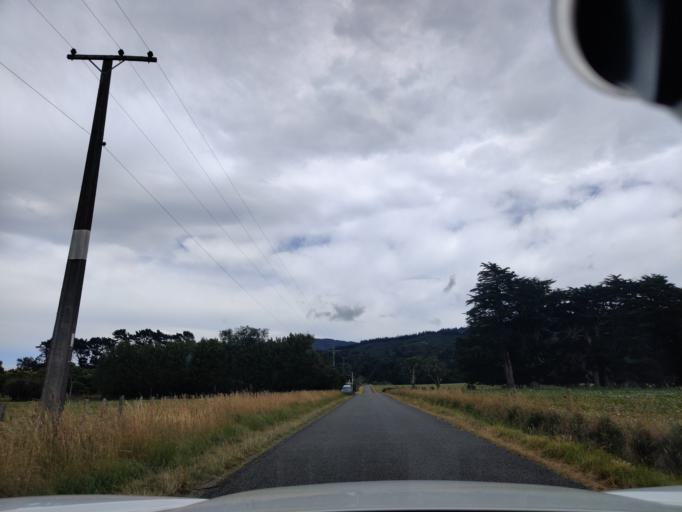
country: NZ
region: Wellington
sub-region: Masterton District
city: Masterton
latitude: -41.0367
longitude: 175.4309
